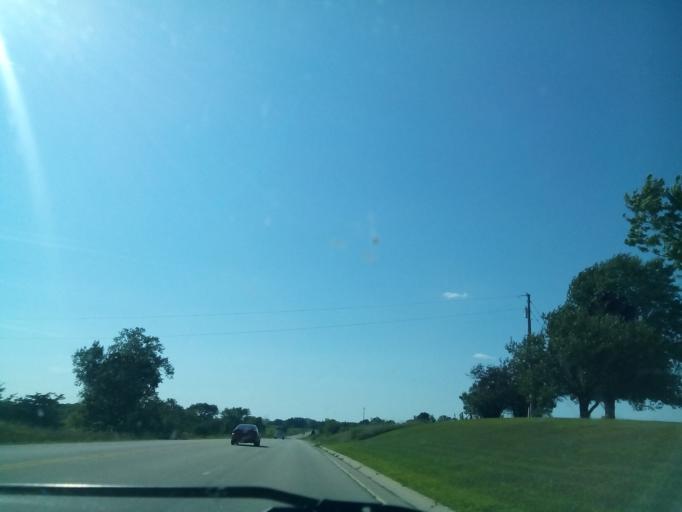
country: US
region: Wisconsin
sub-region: Dane County
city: Belleville
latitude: 42.8623
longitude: -89.5857
